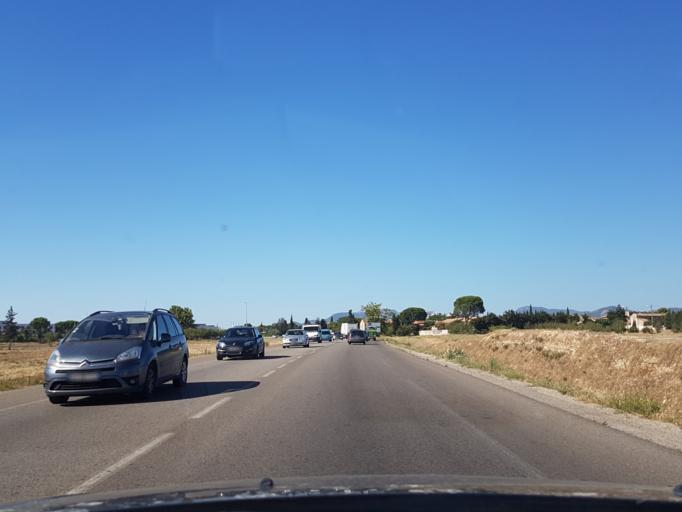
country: FR
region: Provence-Alpes-Cote d'Azur
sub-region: Departement du Vaucluse
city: Carpentras
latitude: 44.0425
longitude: 5.0303
